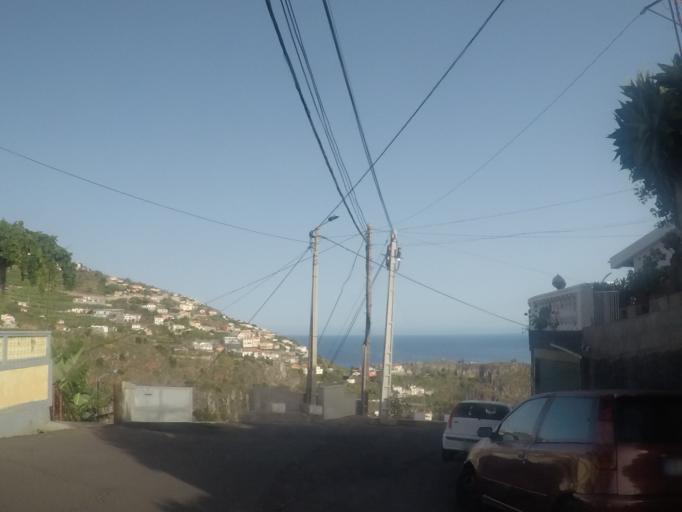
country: PT
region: Madeira
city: Ribeira Brava
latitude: 32.6754
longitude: -17.0664
